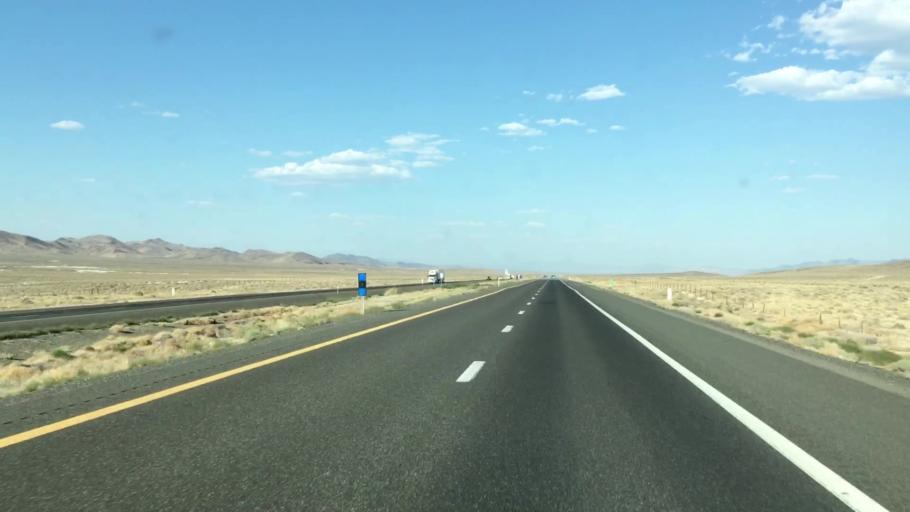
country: US
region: Nevada
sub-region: Lyon County
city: Fernley
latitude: 39.8377
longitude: -118.9555
